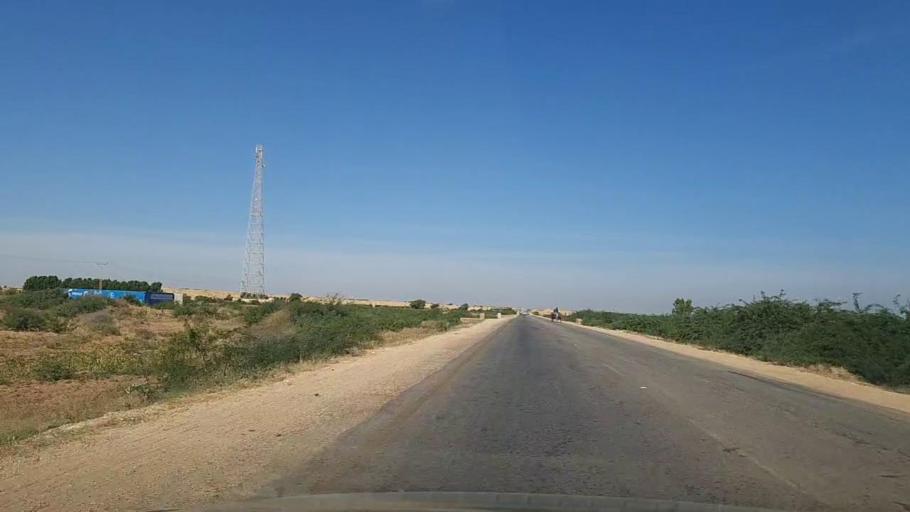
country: PK
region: Sindh
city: Kotri
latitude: 25.2044
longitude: 68.2374
